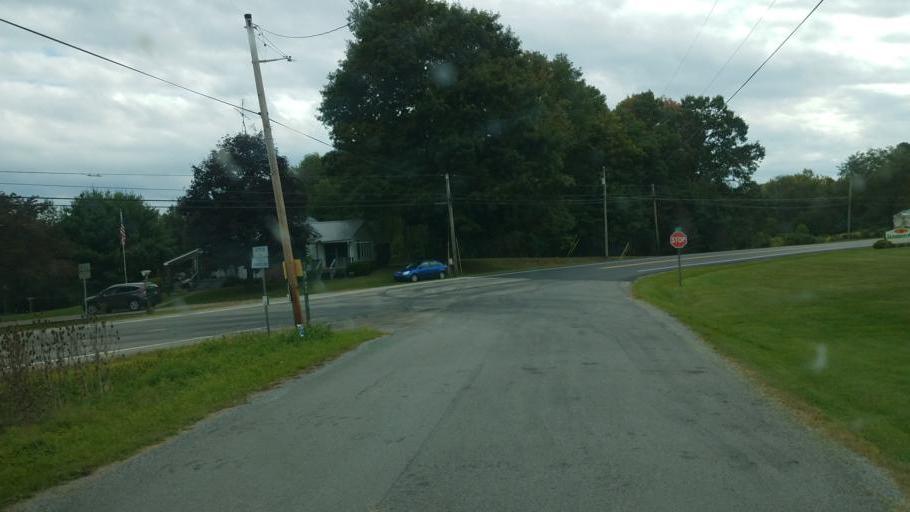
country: US
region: Pennsylvania
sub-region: Mercer County
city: Greenville
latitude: 41.4873
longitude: -80.4474
